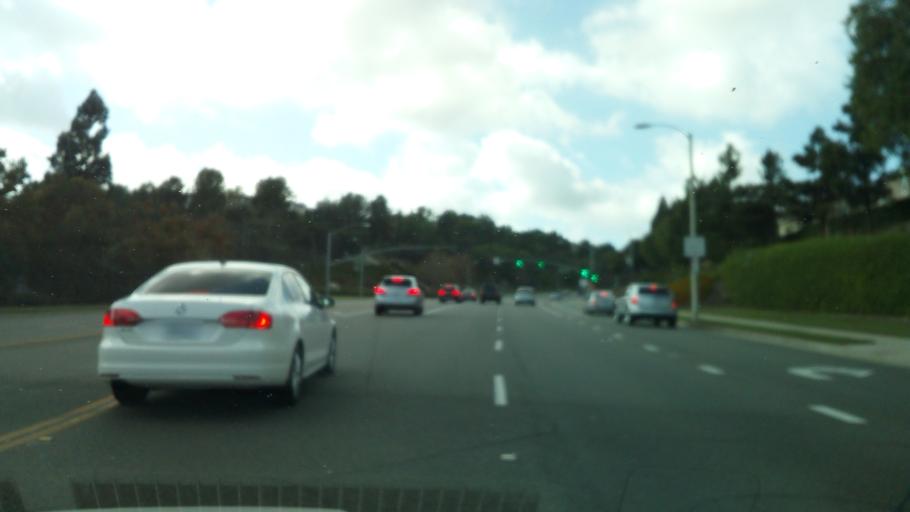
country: US
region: California
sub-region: Orange County
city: Aliso Viejo
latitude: 33.5712
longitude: -117.7338
